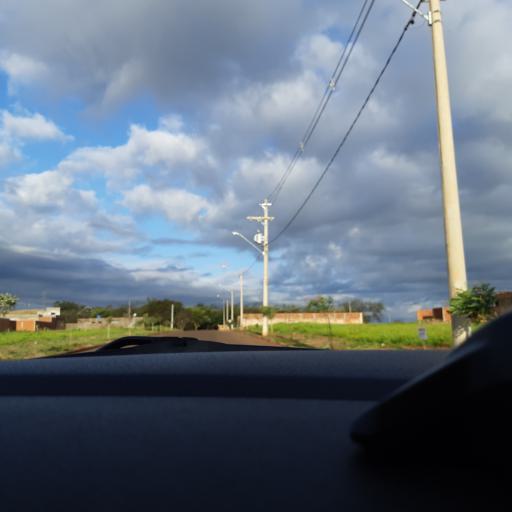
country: BR
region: Sao Paulo
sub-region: Ourinhos
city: Ourinhos
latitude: -23.0042
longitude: -49.8407
